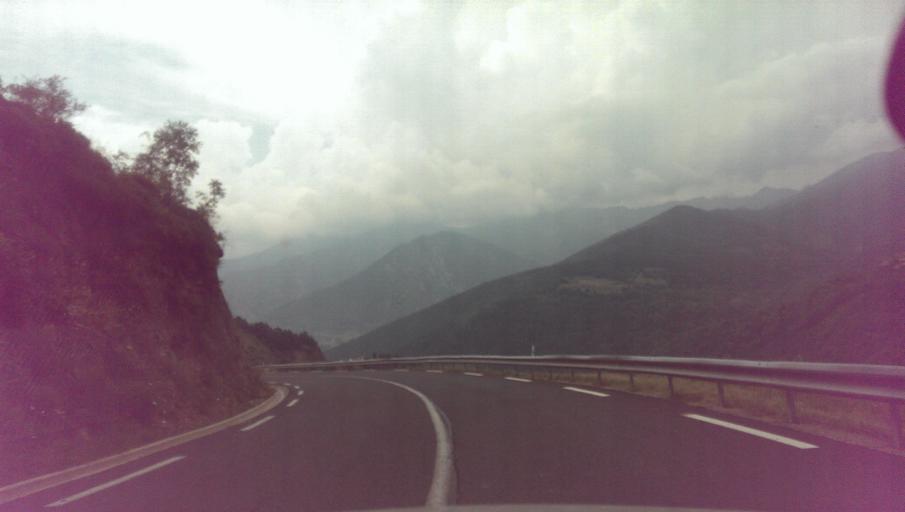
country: ES
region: Catalonia
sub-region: Provincia de Girona
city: Llivia
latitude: 42.5086
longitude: 2.1384
